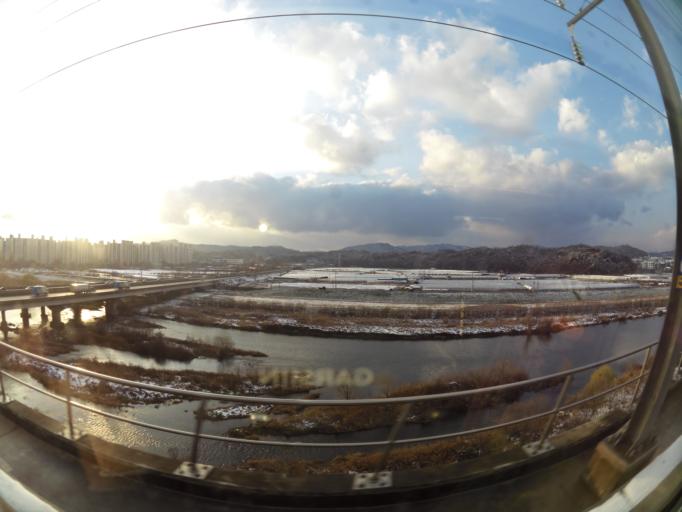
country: KR
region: Daejeon
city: Songgang-dong
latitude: 36.4058
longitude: 127.4149
